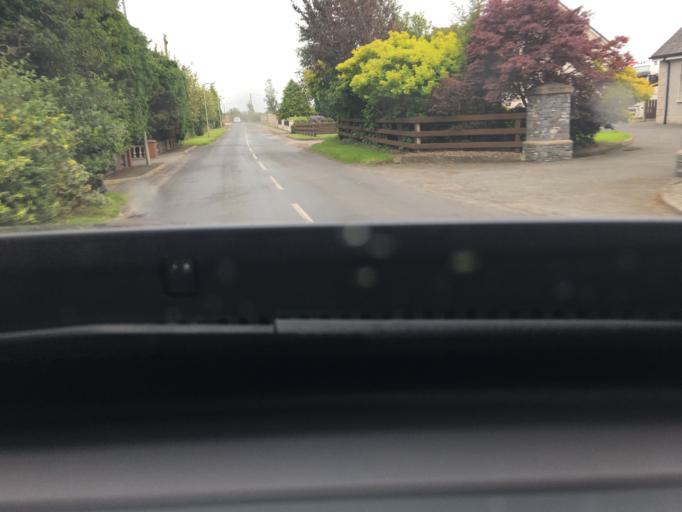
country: GB
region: Northern Ireland
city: Coalisland
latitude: 54.5388
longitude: -6.6221
